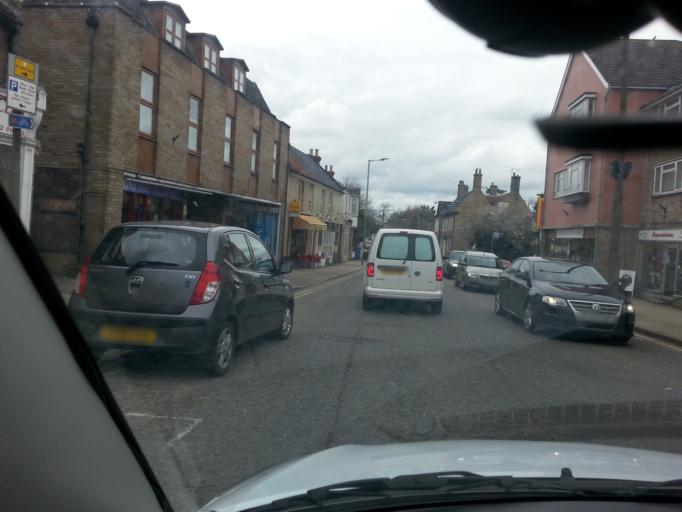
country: GB
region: England
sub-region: Norfolk
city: Weeting
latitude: 52.4490
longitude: 0.6235
